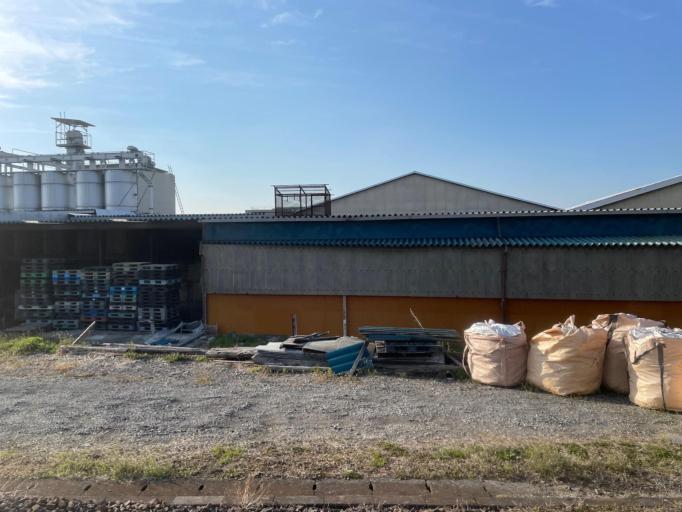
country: JP
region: Gunma
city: Annaka
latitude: 36.3272
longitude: 138.9047
